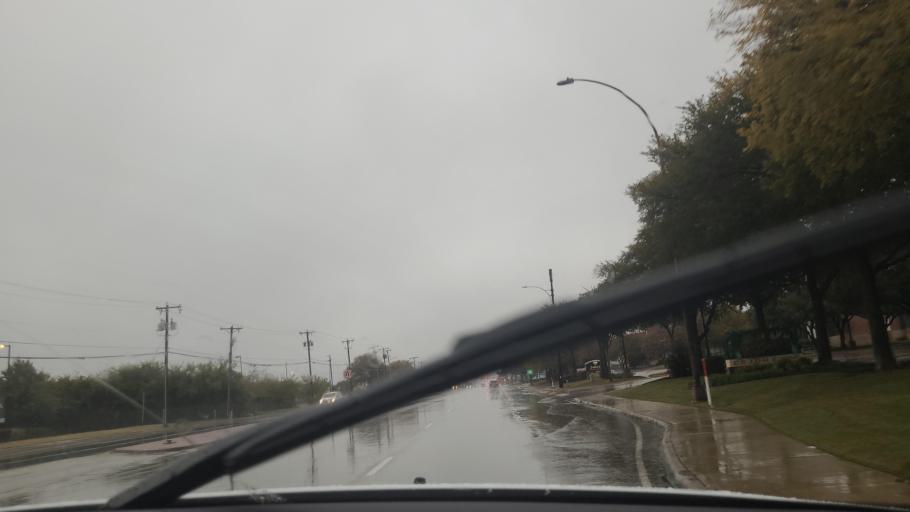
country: US
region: Texas
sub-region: Tarrant County
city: Dalworthington Gardens
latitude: 32.6810
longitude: -97.1341
